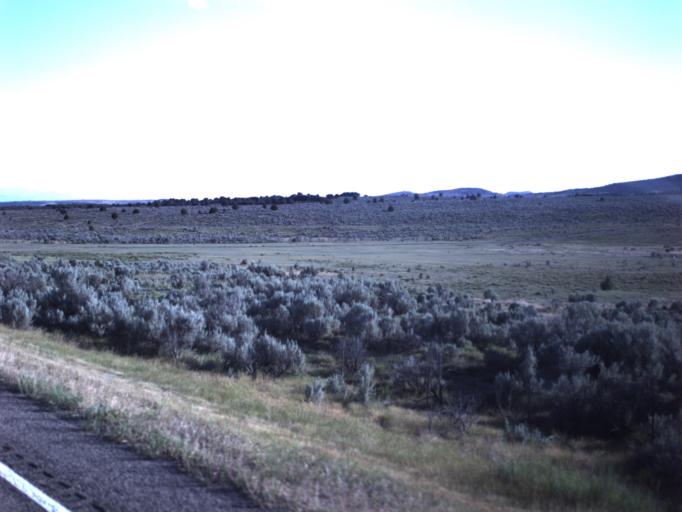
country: US
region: Utah
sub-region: Sanpete County
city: Fairview
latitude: 39.6837
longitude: -111.4585
